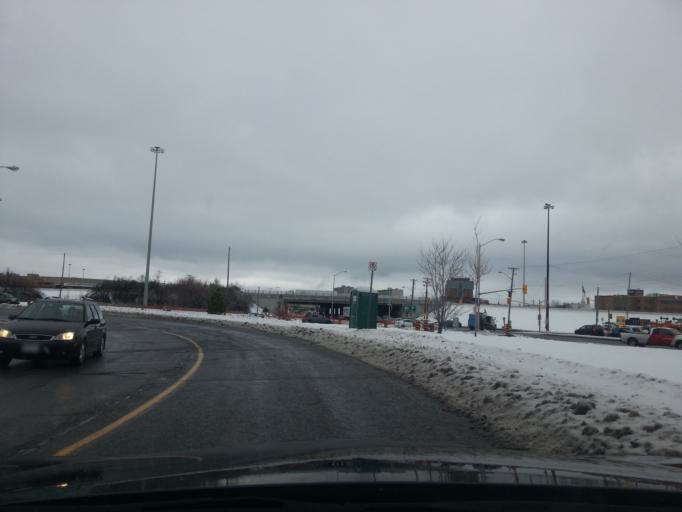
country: CA
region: Ontario
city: Ottawa
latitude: 45.4184
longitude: -75.6347
